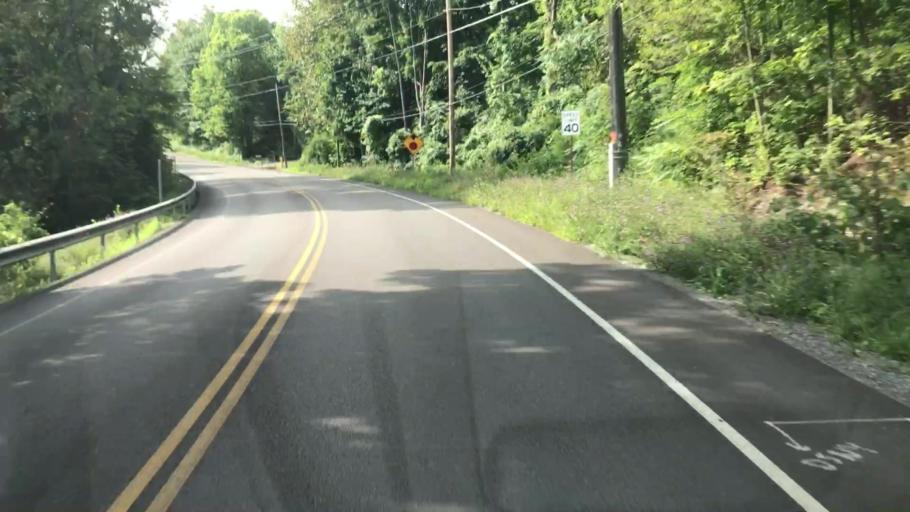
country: US
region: New York
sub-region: Onondaga County
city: Fayetteville
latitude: 43.0115
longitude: -76.0122
